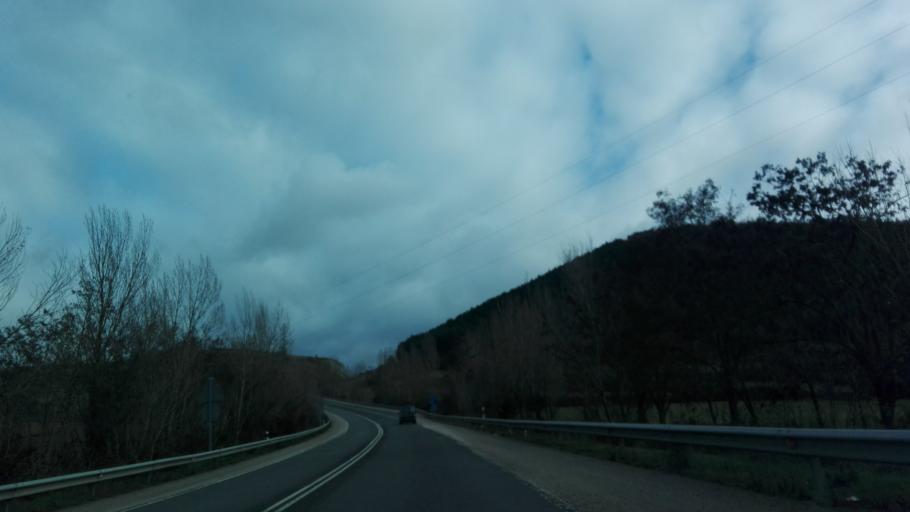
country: ES
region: Navarre
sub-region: Provincia de Navarra
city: Atarrabia
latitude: 42.8385
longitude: -1.6056
